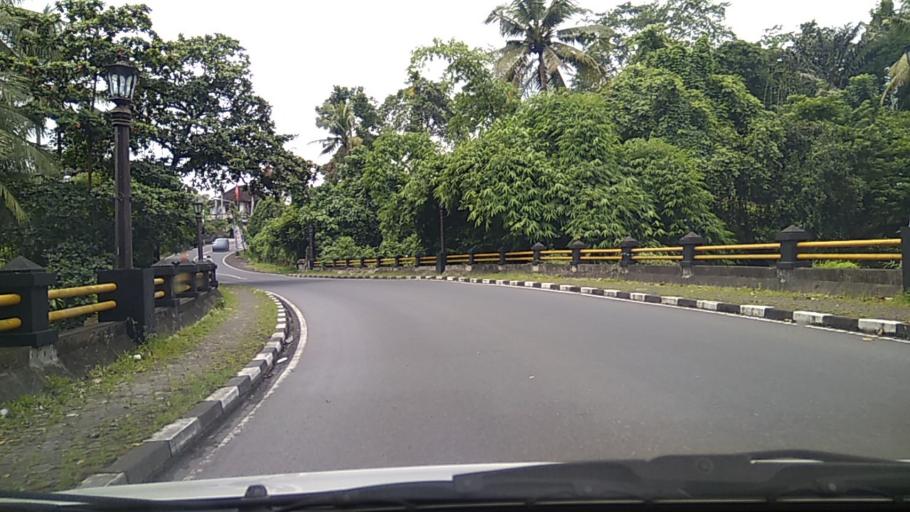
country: ID
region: Bali
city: Banjar Tebongkang
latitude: -8.5275
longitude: 115.2548
